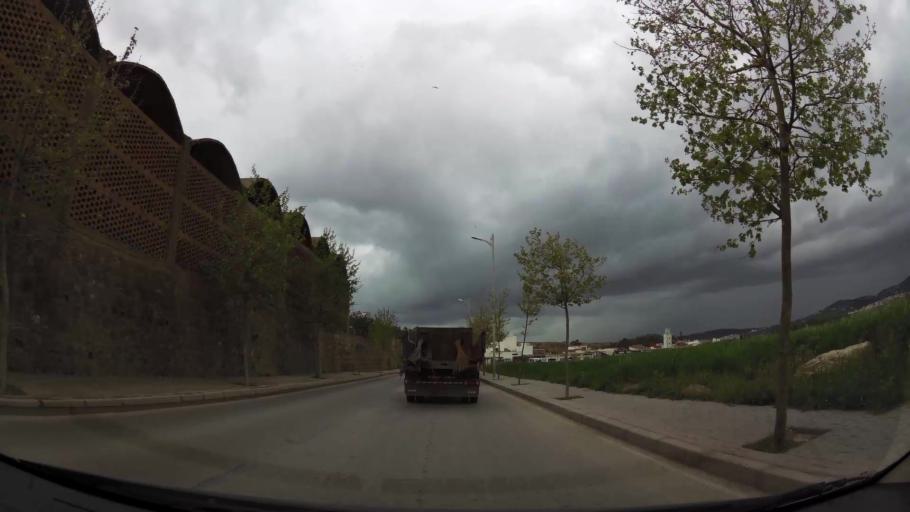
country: MA
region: Tanger-Tetouan
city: Tetouan
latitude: 35.5554
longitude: -5.3961
